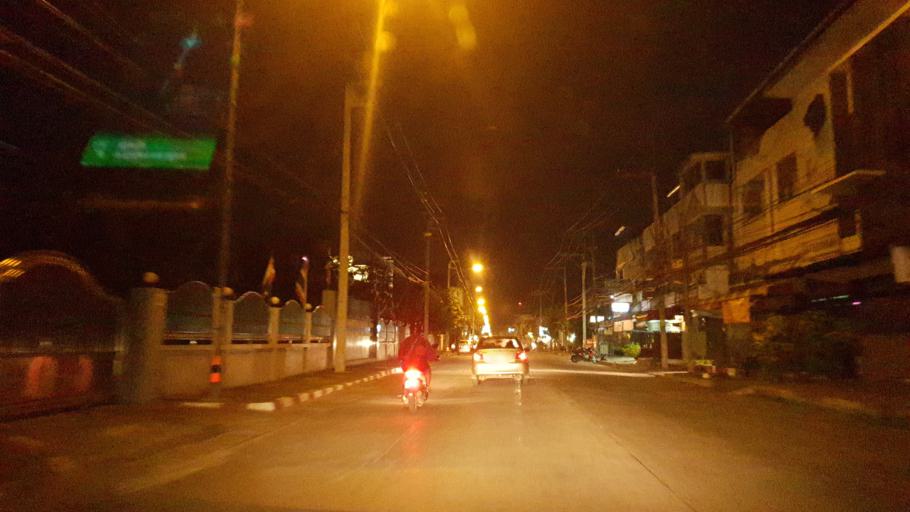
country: TH
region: Phitsanulok
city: Phitsanulok
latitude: 16.8068
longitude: 100.2697
